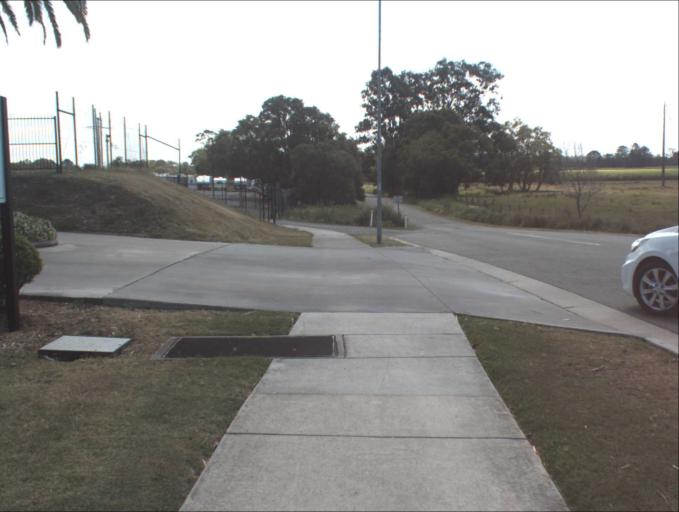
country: AU
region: Queensland
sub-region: Logan
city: Beenleigh
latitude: -27.6868
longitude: 153.2131
